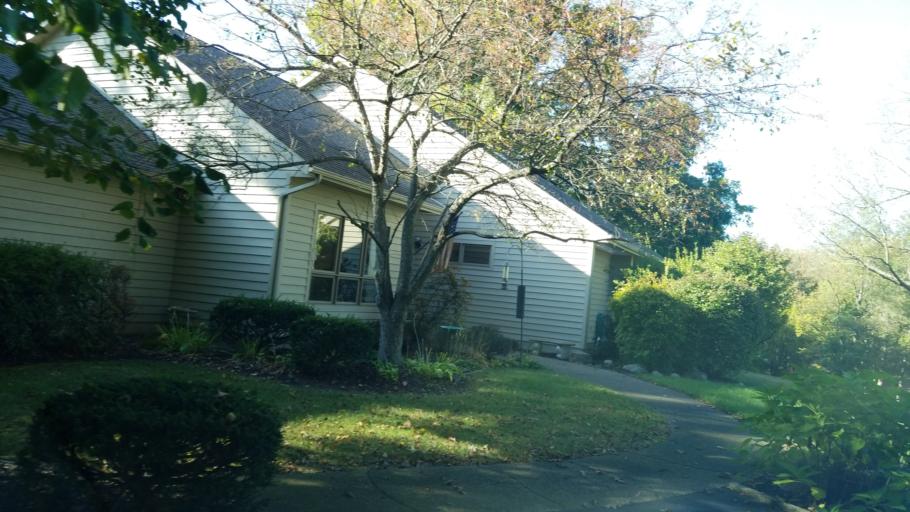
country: US
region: Ohio
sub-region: Licking County
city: Utica
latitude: 40.1665
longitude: -82.3792
